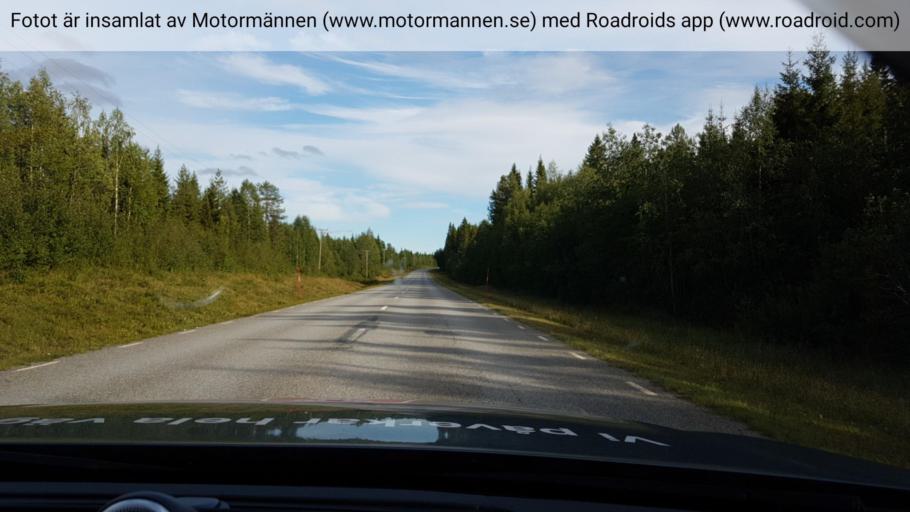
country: SE
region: Jaemtland
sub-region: Stroemsunds Kommun
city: Stroemsund
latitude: 64.2977
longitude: 15.3256
